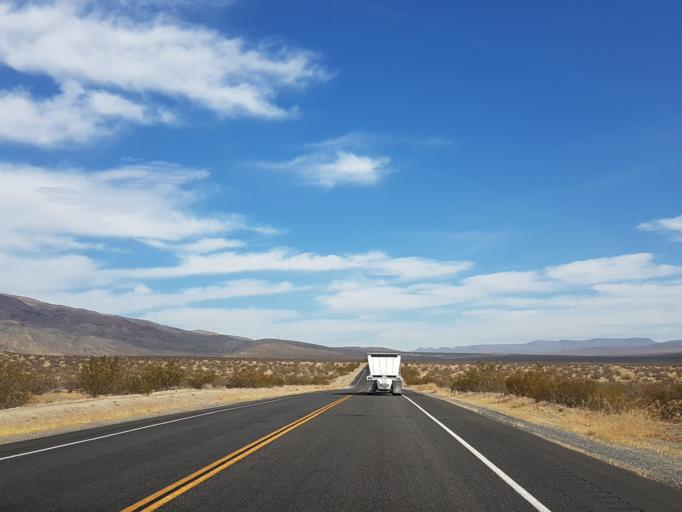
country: US
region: California
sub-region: Kern County
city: Ridgecrest
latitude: 35.4199
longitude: -117.7446
